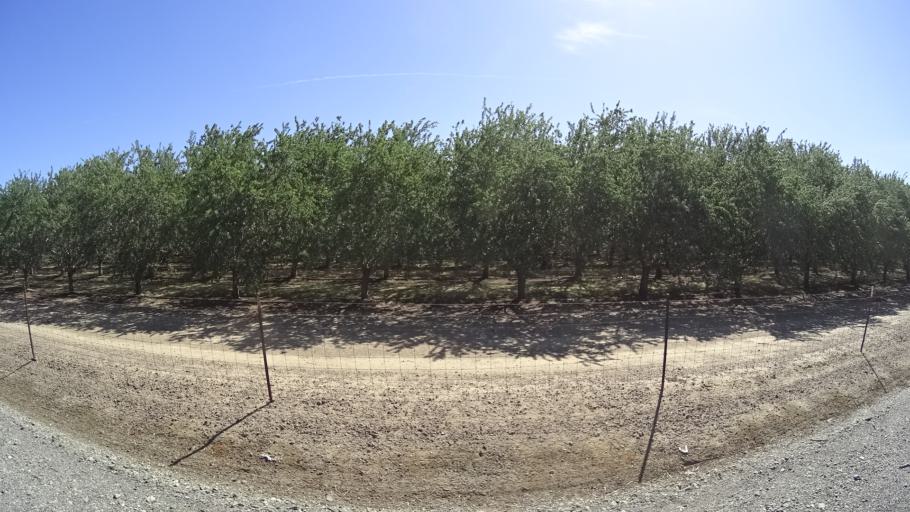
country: US
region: California
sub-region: Glenn County
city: Hamilton City
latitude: 39.6608
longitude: -122.1035
